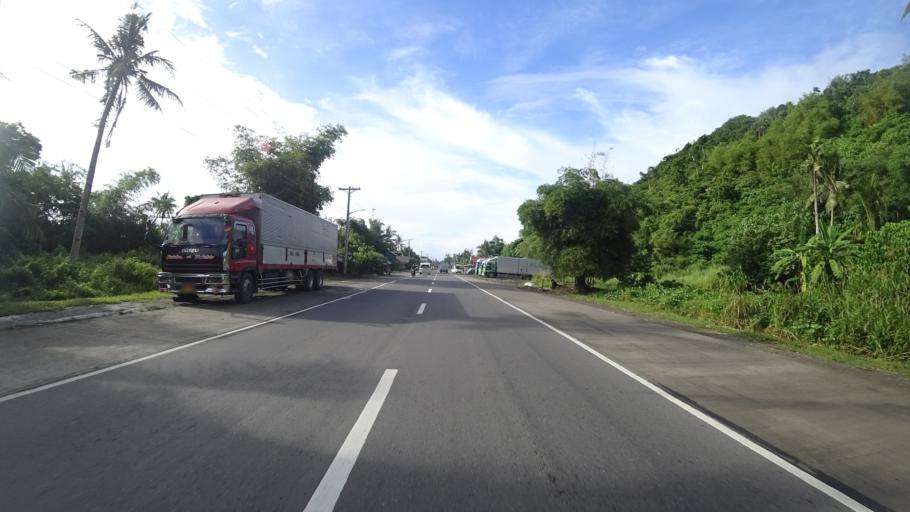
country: PH
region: Eastern Visayas
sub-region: Province of Leyte
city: Kabuynan
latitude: 11.0897
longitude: 125.0216
